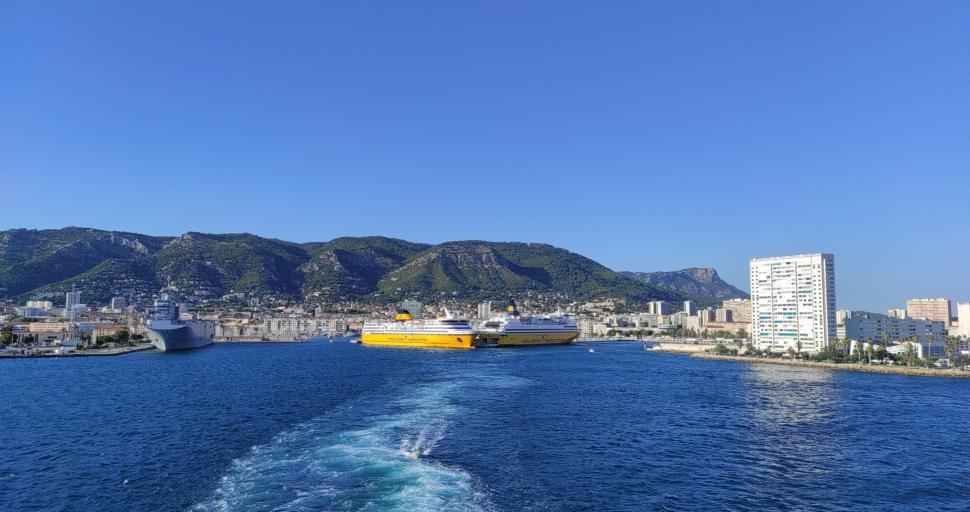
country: FR
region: Provence-Alpes-Cote d'Azur
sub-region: Departement du Var
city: Toulon
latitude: 43.1109
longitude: 5.9259
